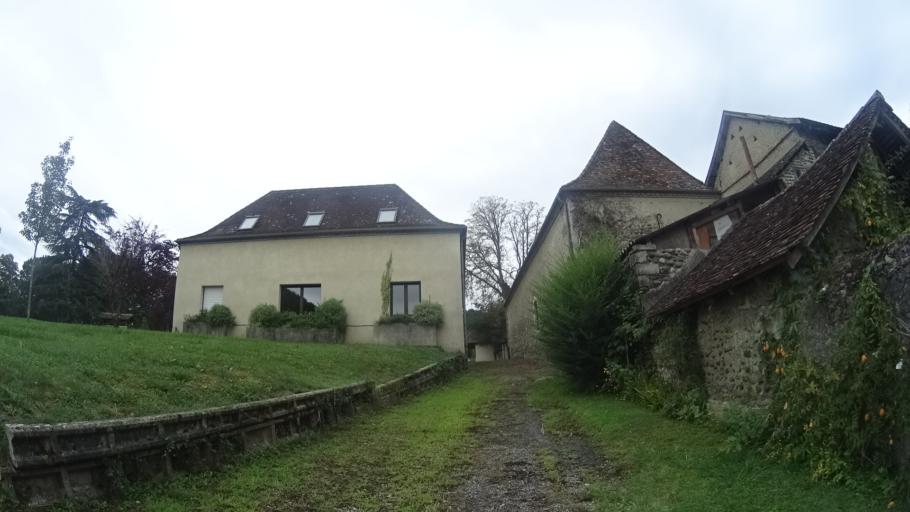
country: FR
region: Aquitaine
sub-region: Departement des Pyrenees-Atlantiques
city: Orthez
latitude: 43.4688
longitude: -0.7130
